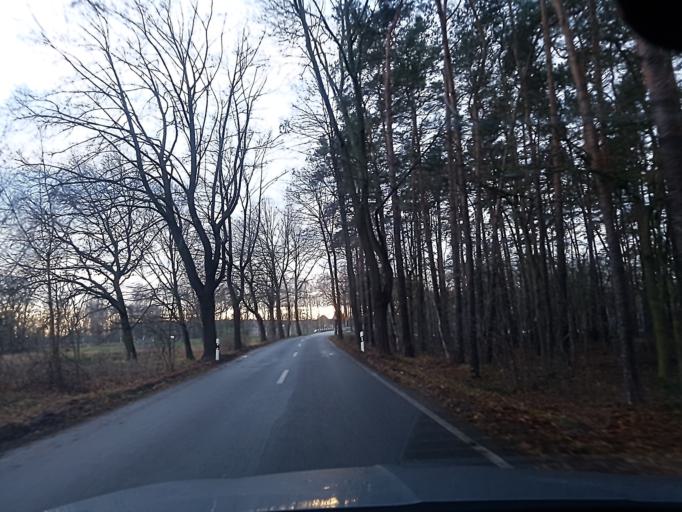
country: DE
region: Brandenburg
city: Schilda
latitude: 51.5727
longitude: 13.3536
